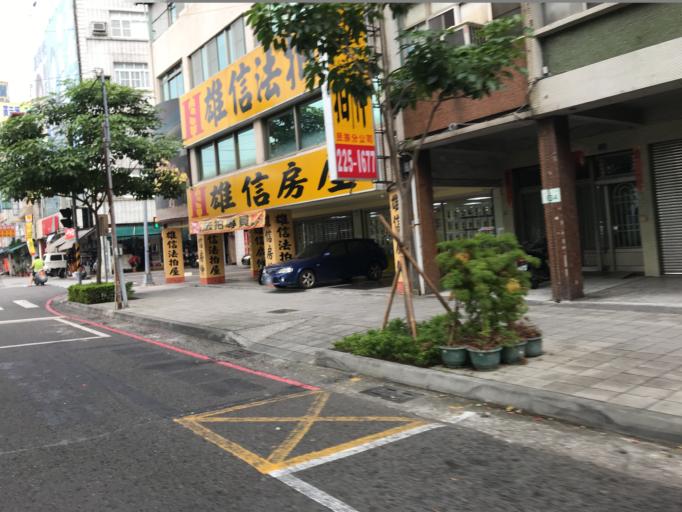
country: TW
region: Kaohsiung
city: Kaohsiung
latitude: 22.6349
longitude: 120.3138
